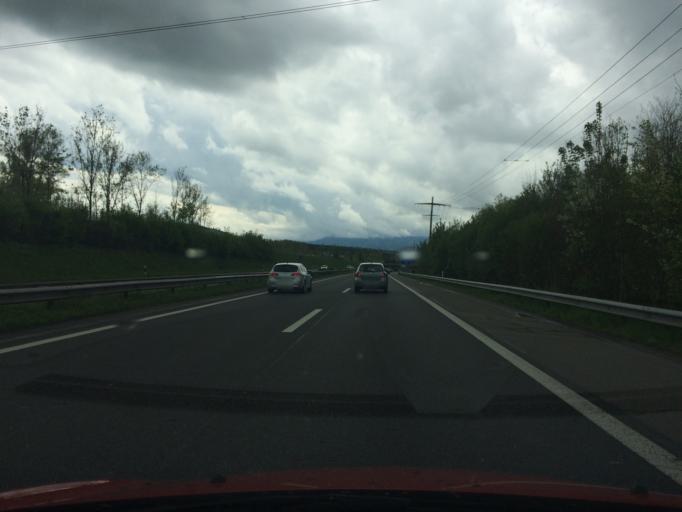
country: CH
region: Lucerne
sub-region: Lucerne-Land District
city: Buchrain
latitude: 47.1079
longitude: 8.3498
